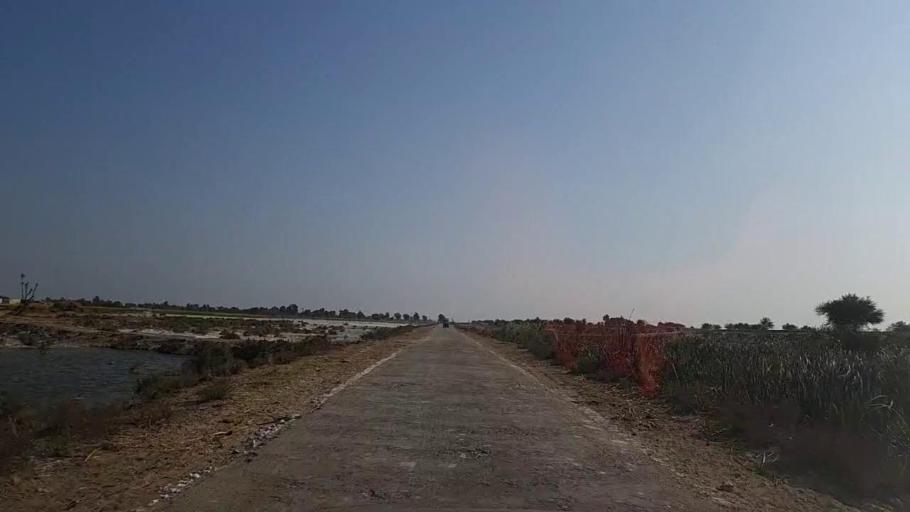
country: PK
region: Sindh
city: Sanghar
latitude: 25.9766
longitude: 69.0268
